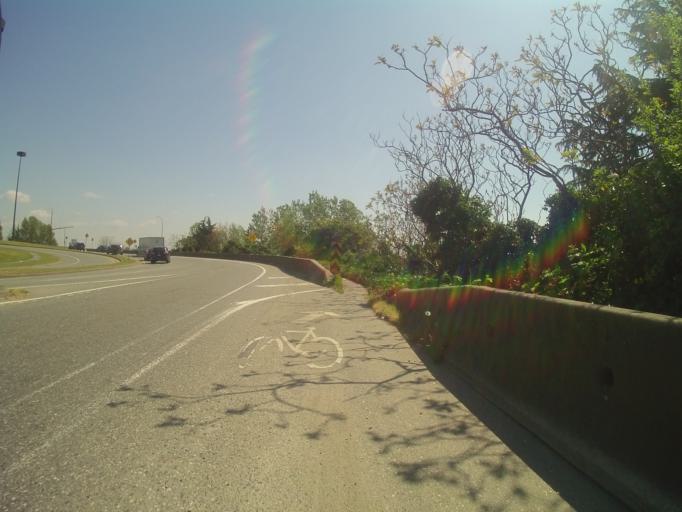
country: CA
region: British Columbia
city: Vancouver
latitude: 49.2105
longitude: -123.0790
